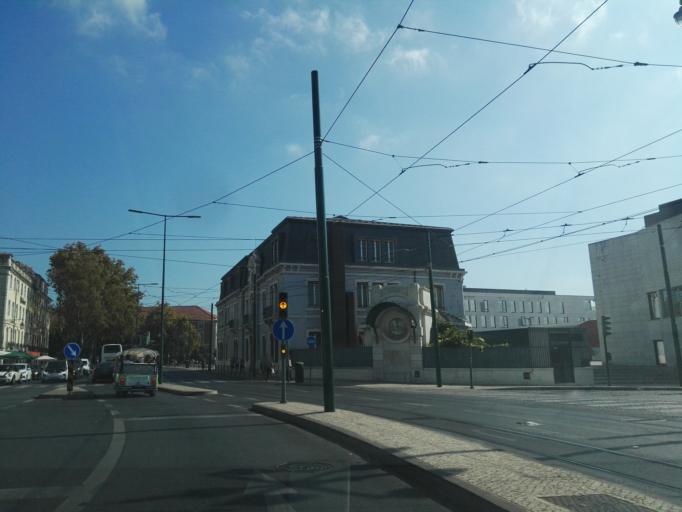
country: PT
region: Lisbon
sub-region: Lisbon
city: Lisbon
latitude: 38.7063
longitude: -9.1434
